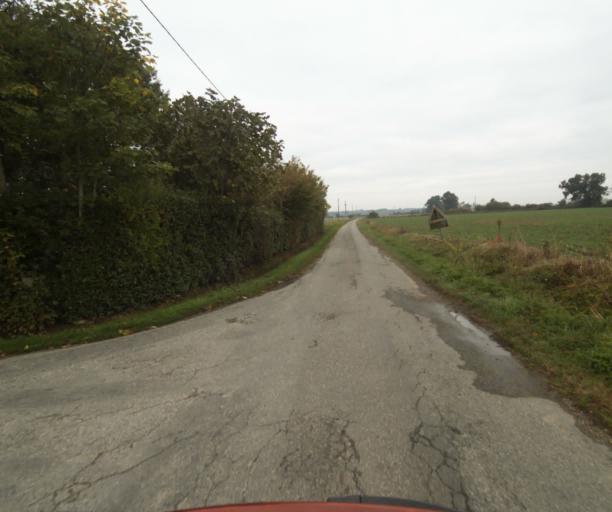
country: FR
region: Midi-Pyrenees
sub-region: Departement du Tarn-et-Garonne
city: Verdun-sur-Garonne
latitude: 43.8137
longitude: 1.2309
